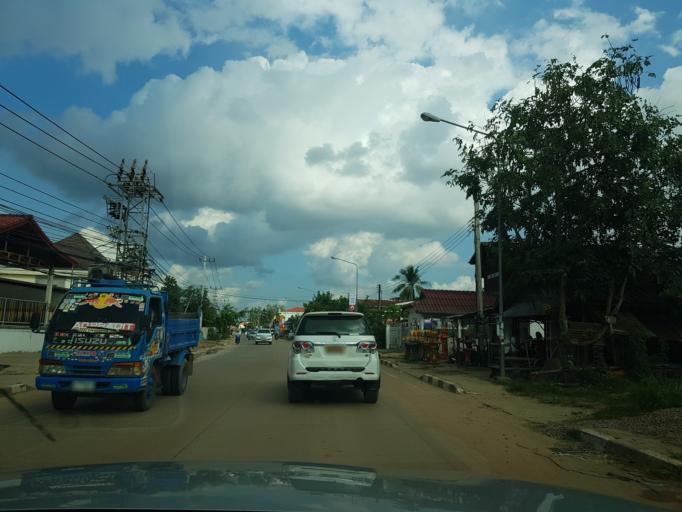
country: TH
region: Nong Khai
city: Si Chiang Mai
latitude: 17.9777
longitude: 102.5299
